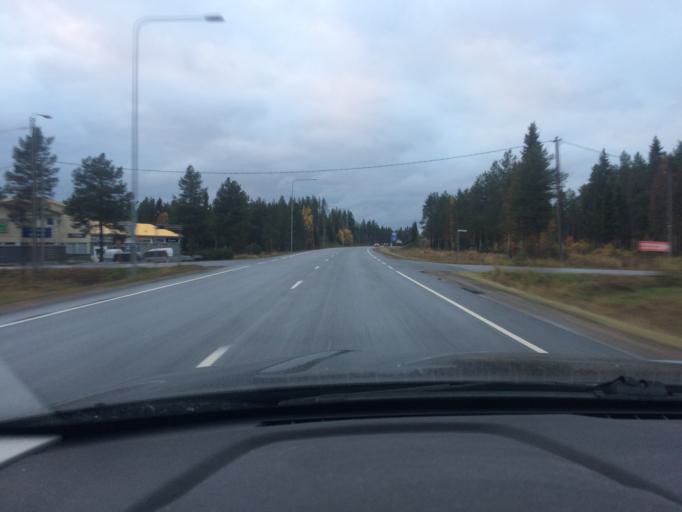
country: FI
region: Northern Ostrobothnia
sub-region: Koillismaa
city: Kuusamo
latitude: 65.9894
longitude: 29.1578
